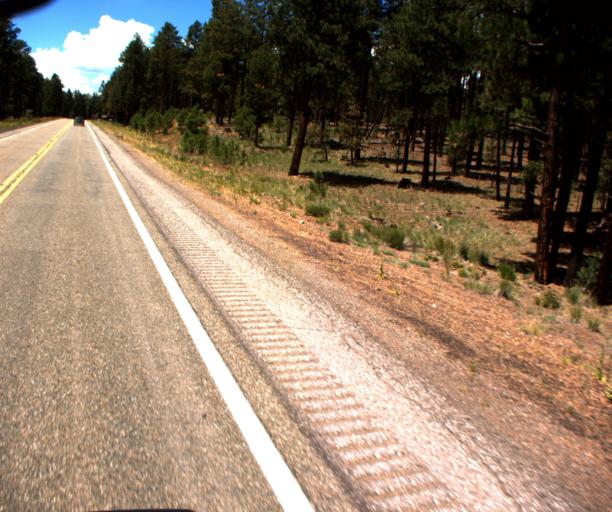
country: US
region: Arizona
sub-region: Coconino County
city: Flagstaff
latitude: 35.2852
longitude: -111.7538
